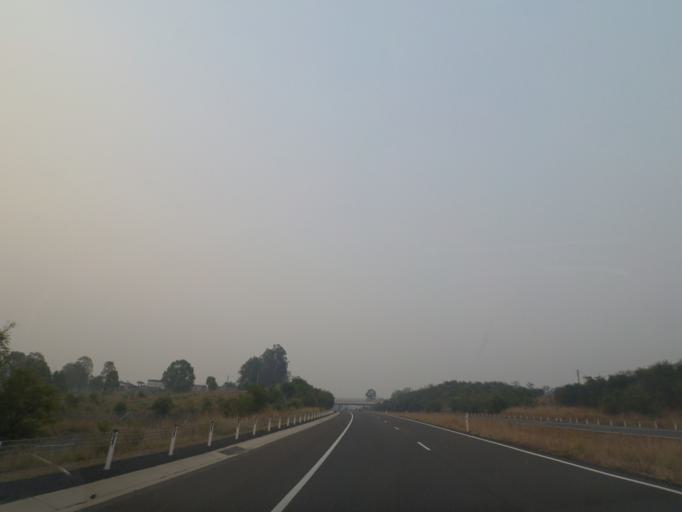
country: AU
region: New South Wales
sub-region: Nambucca Shire
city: Macksville
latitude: -30.7666
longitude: 152.9034
